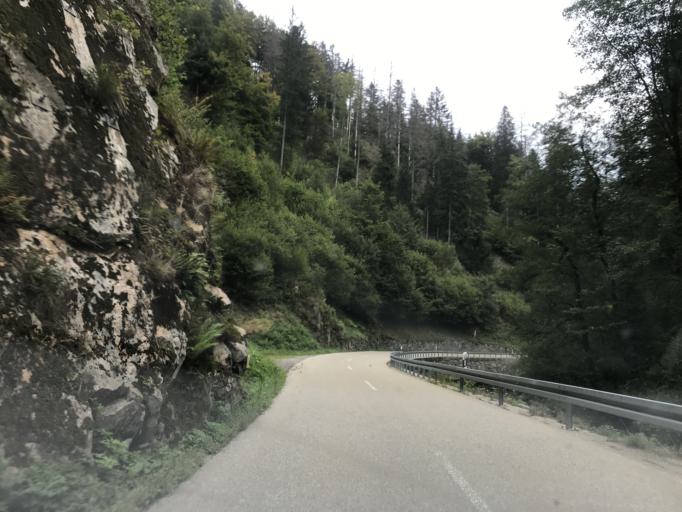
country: DE
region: Baden-Wuerttemberg
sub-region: Freiburg Region
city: Herrischried
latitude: 47.6870
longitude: 7.9630
